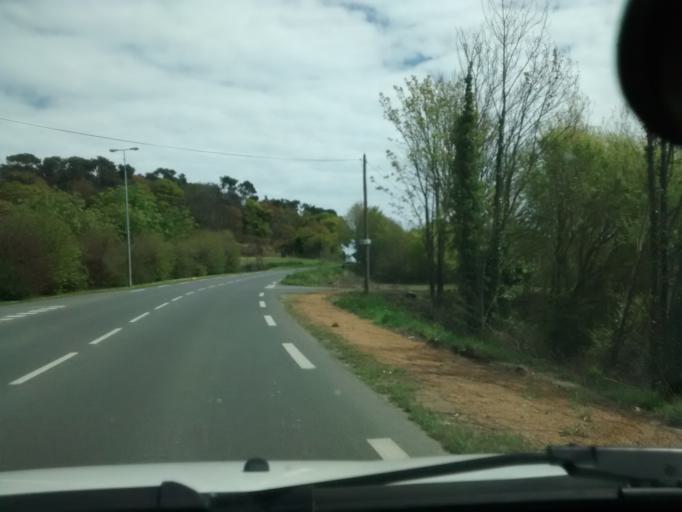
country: FR
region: Brittany
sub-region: Departement des Cotes-d'Armor
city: Ploubazlanec
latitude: 48.7926
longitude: -3.0412
